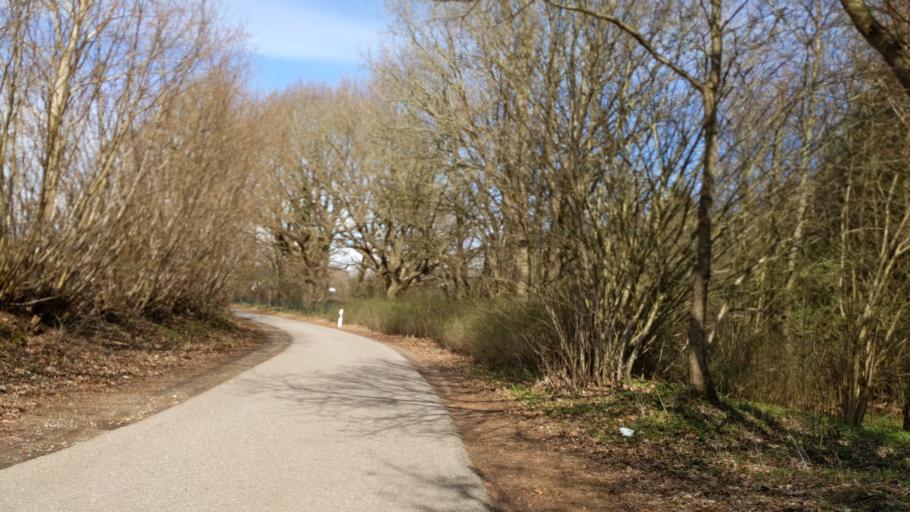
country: DE
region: Schleswig-Holstein
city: Ratekau
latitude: 53.9849
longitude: 10.6796
